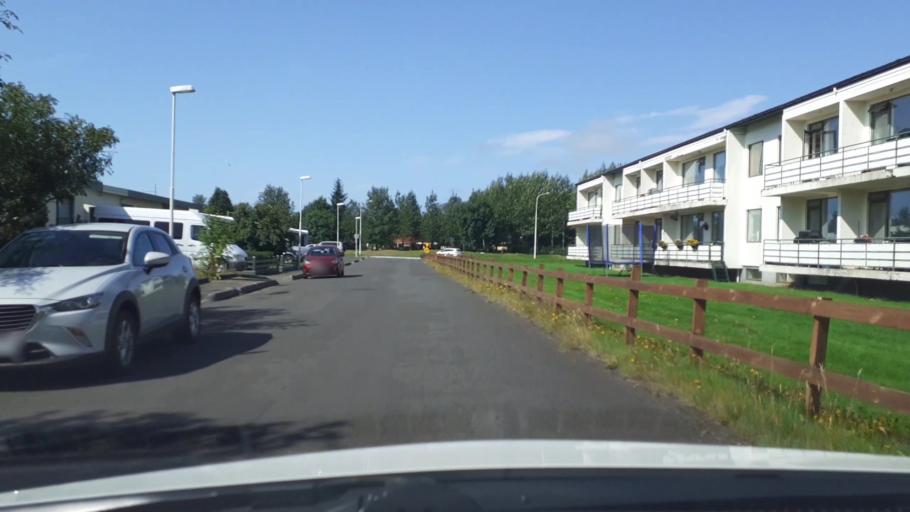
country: IS
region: South
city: Selfoss
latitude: 63.9313
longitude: -21.0027
